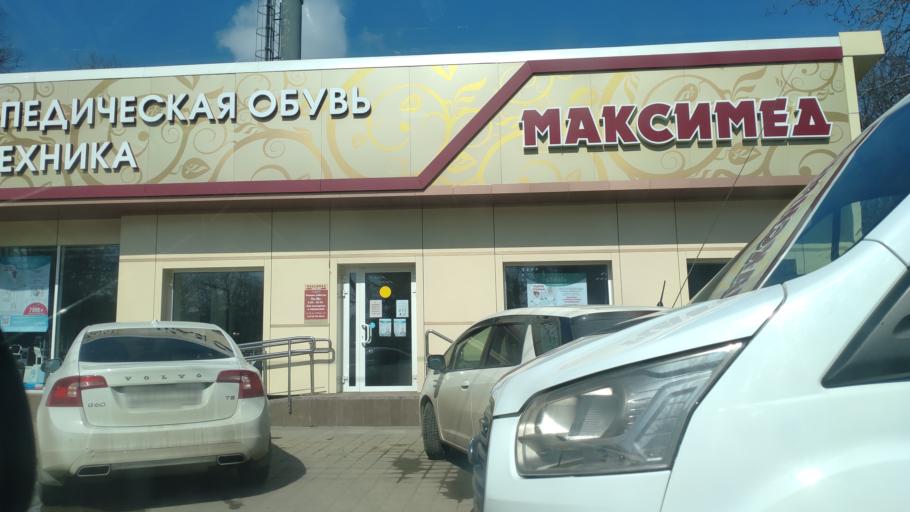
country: RU
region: Krasnodarskiy
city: Krasnodar
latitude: 45.0548
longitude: 38.9953
